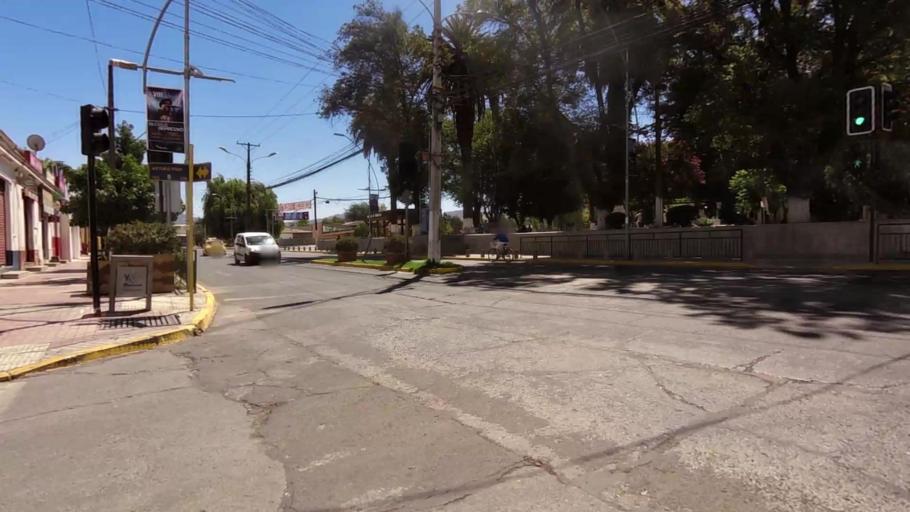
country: CL
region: O'Higgins
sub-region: Provincia de Cachapoal
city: Graneros
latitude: -33.9801
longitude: -70.7126
